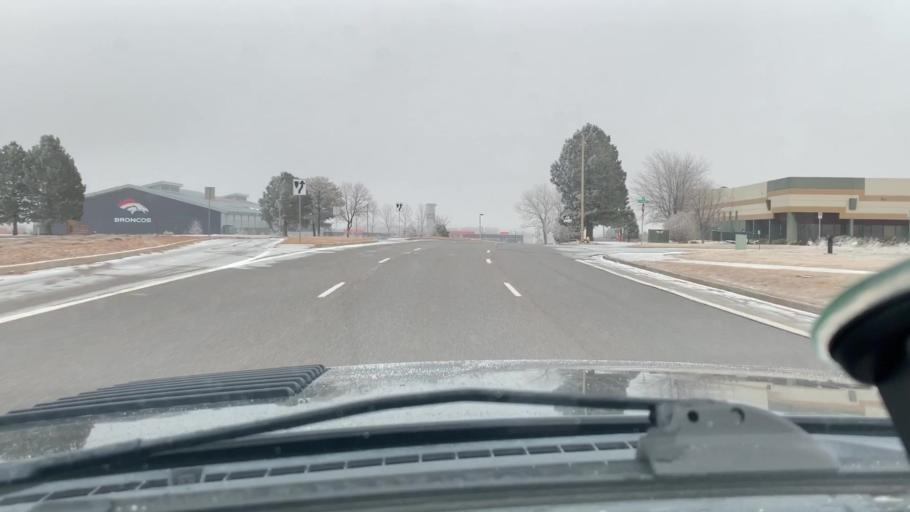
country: US
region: Colorado
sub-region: Arapahoe County
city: Dove Valley
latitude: 39.5787
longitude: -104.8365
